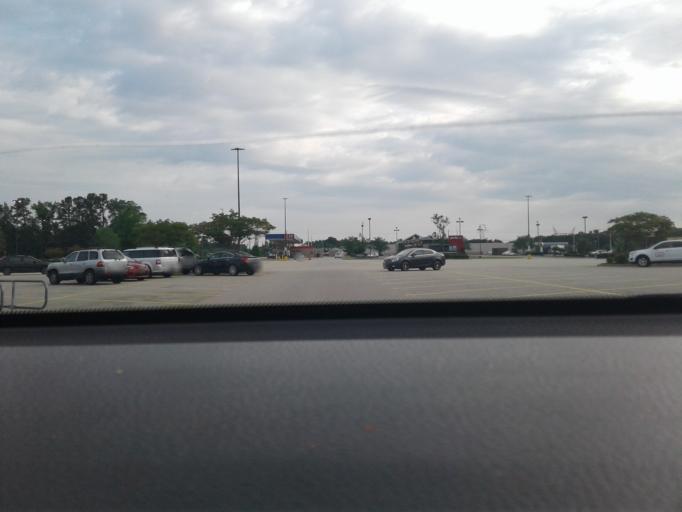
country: US
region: North Carolina
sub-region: Harnett County
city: Erwin
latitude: 35.3218
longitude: -78.6479
